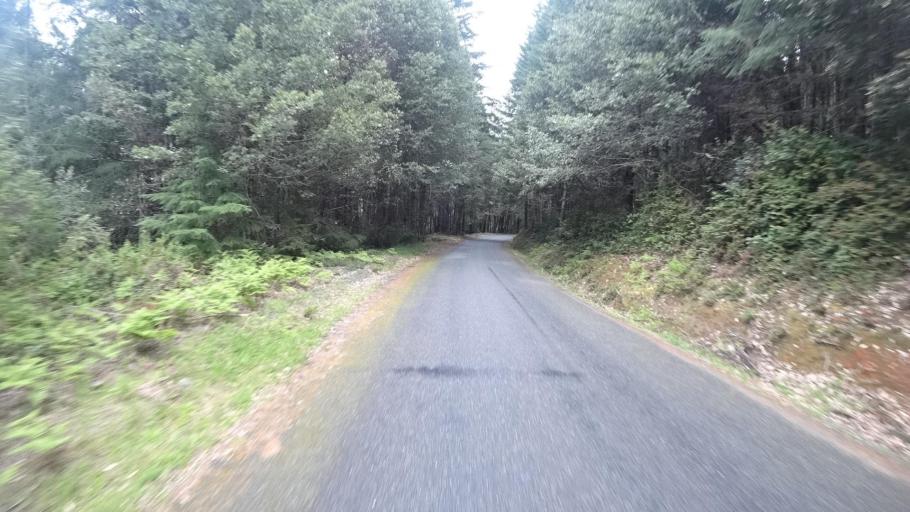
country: US
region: California
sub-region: Humboldt County
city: Willow Creek
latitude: 41.2004
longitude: -123.7710
